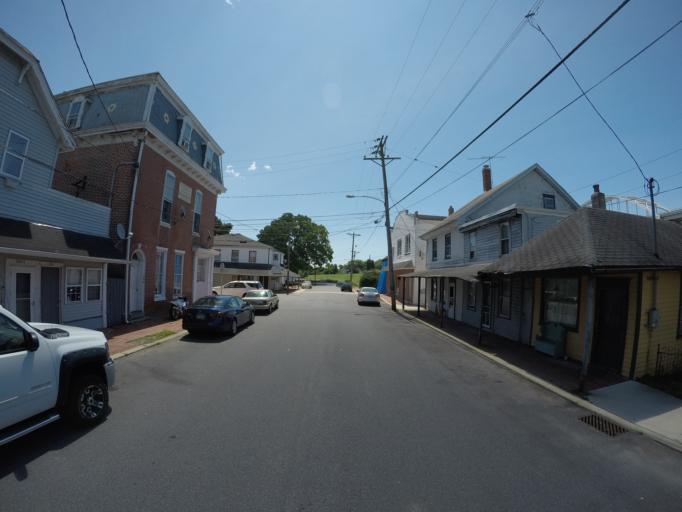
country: US
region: Delaware
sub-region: New Castle County
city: Delaware City
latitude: 39.5552
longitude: -75.6506
